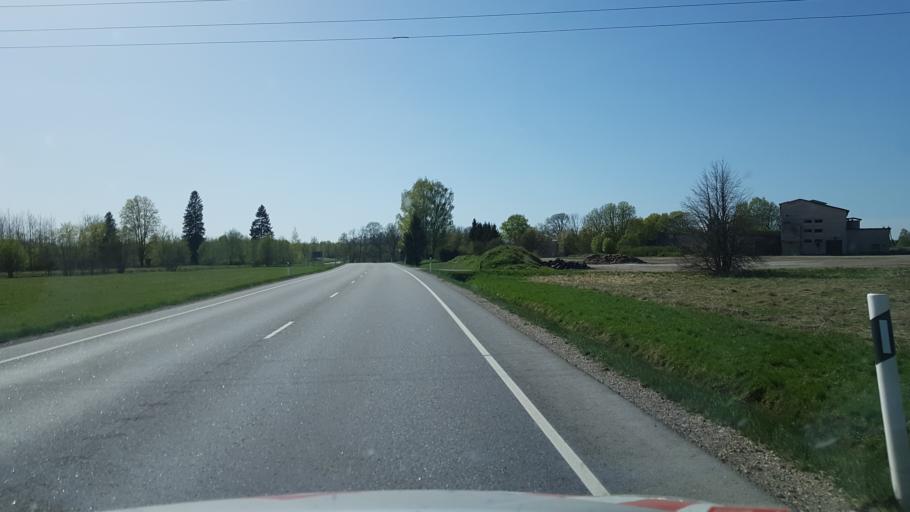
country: EE
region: Viljandimaa
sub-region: Abja vald
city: Abja-Paluoja
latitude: 58.1202
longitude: 25.3750
